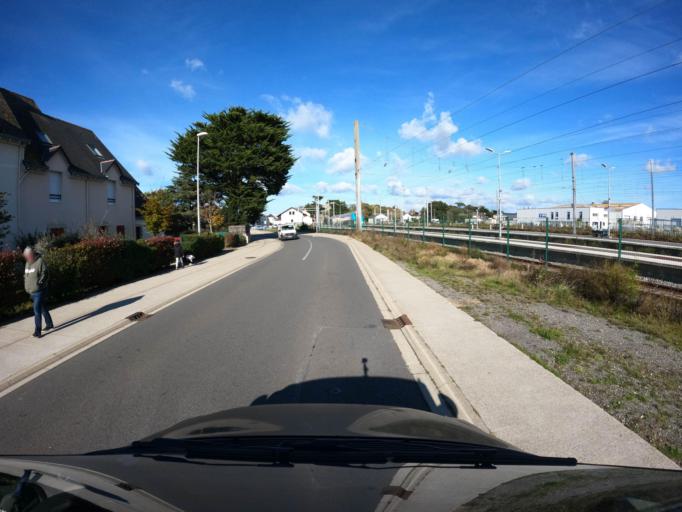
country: FR
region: Pays de la Loire
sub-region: Departement de la Loire-Atlantique
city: Le Croisic
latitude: 47.2884
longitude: -2.5062
